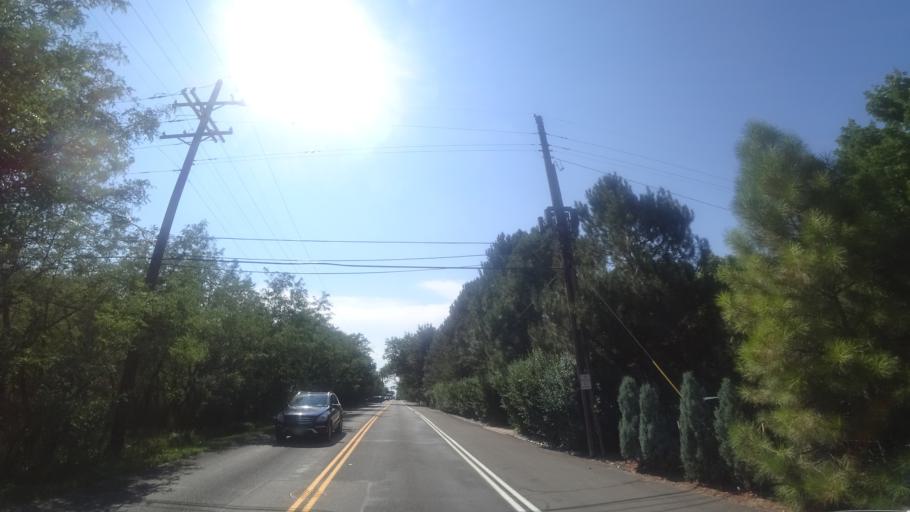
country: US
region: Colorado
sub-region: Arapahoe County
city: Cherry Hills Village
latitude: 39.6387
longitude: -104.9700
